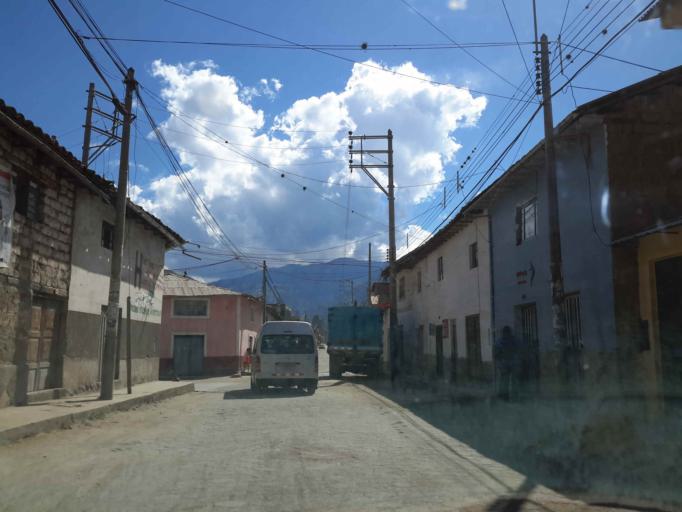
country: PE
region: Apurimac
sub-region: Provincia de Andahuaylas
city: Talavera
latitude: -13.6522
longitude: -73.4317
